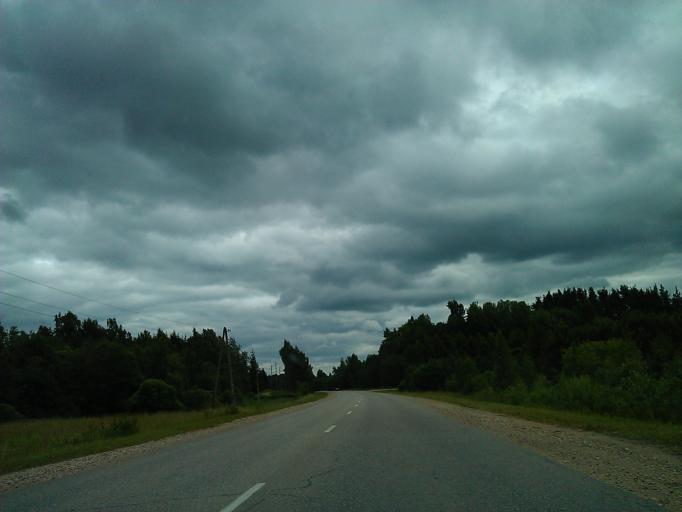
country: LV
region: Kuldigas Rajons
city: Kuldiga
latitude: 56.9641
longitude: 21.9374
